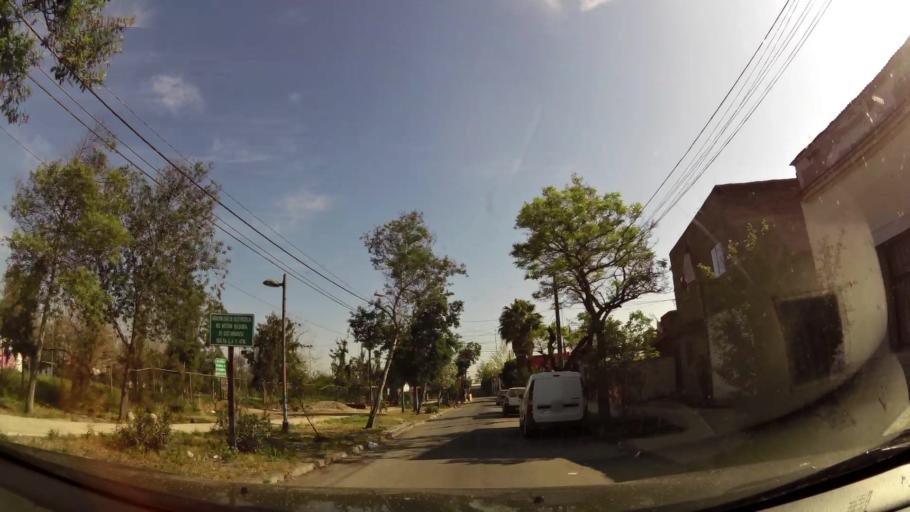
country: CL
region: Santiago Metropolitan
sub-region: Provincia de Santiago
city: Santiago
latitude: -33.4095
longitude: -70.6747
